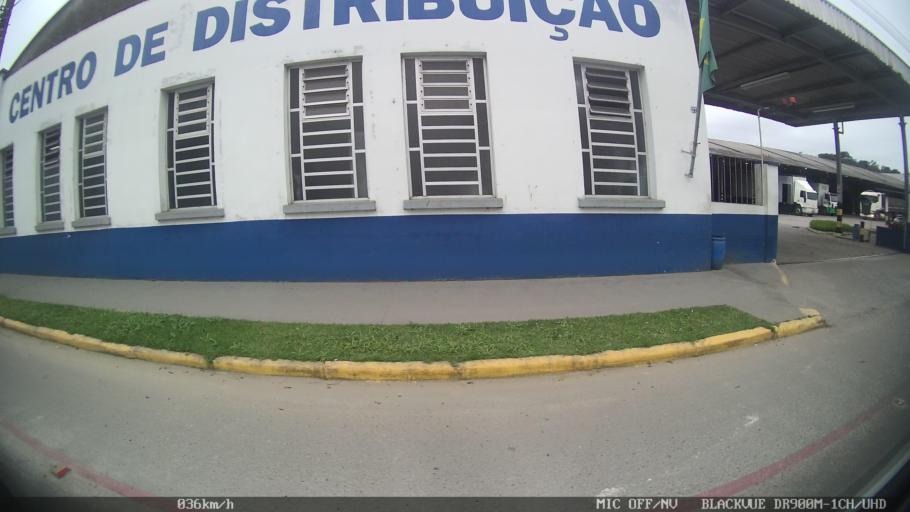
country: BR
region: Santa Catarina
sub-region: Joinville
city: Joinville
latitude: -26.3141
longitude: -48.8342
